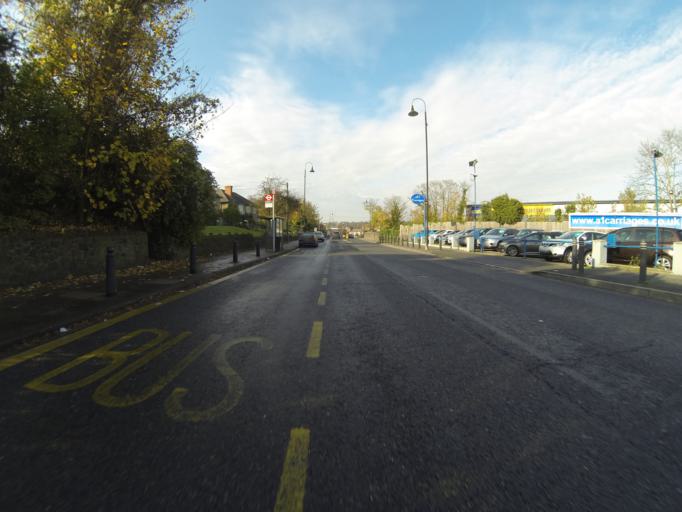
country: GB
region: England
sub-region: Kent
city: Dartford
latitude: 51.4494
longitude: 0.1863
